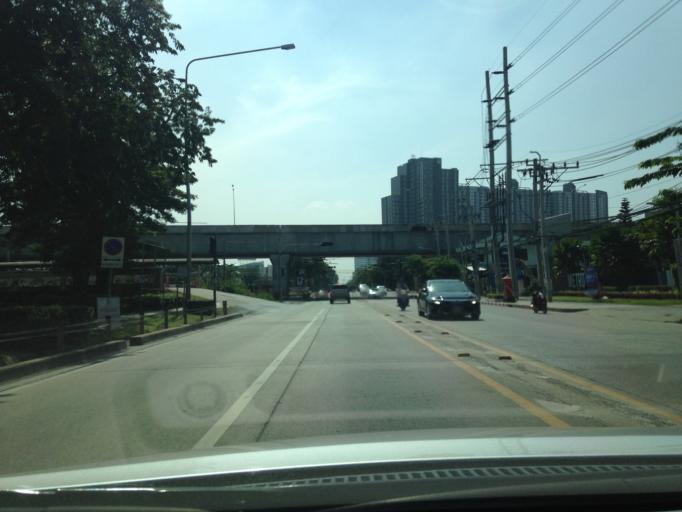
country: TH
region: Bangkok
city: Bang Sue
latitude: 13.8229
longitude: 100.5372
